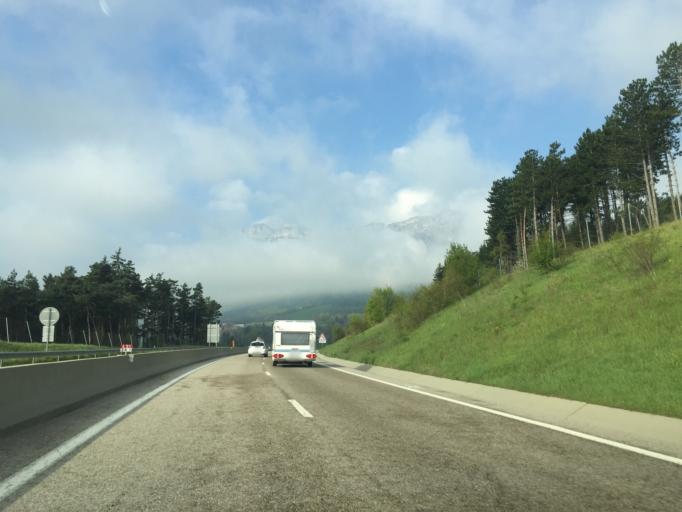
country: FR
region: Rhone-Alpes
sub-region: Departement de l'Isere
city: La Motte-Saint-Martin
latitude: 44.9191
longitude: 5.6282
